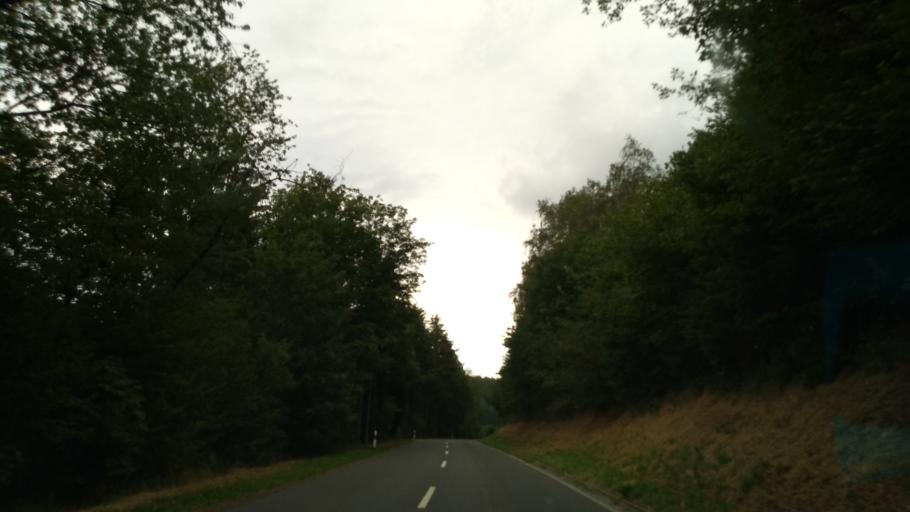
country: DE
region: North Rhine-Westphalia
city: Balve
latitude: 51.3000
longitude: 7.8963
